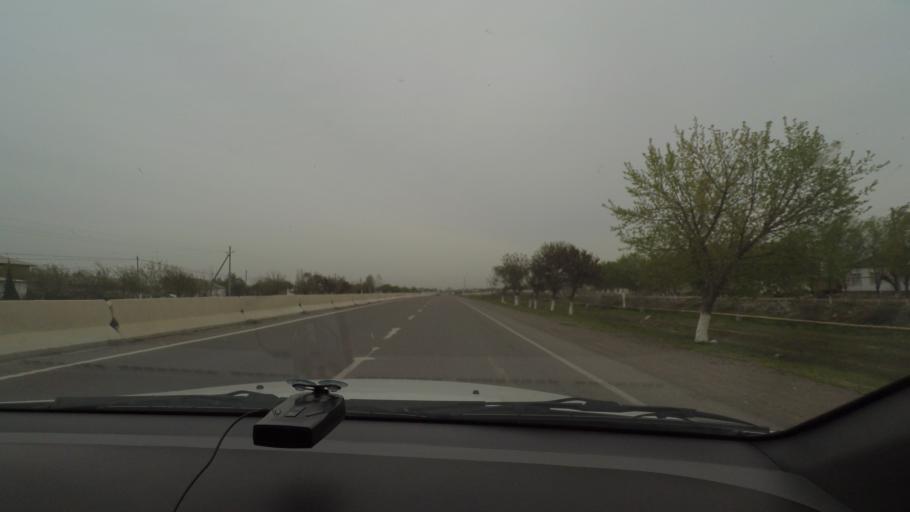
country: UZ
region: Sirdaryo
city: Guliston
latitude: 40.4921
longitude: 68.6912
